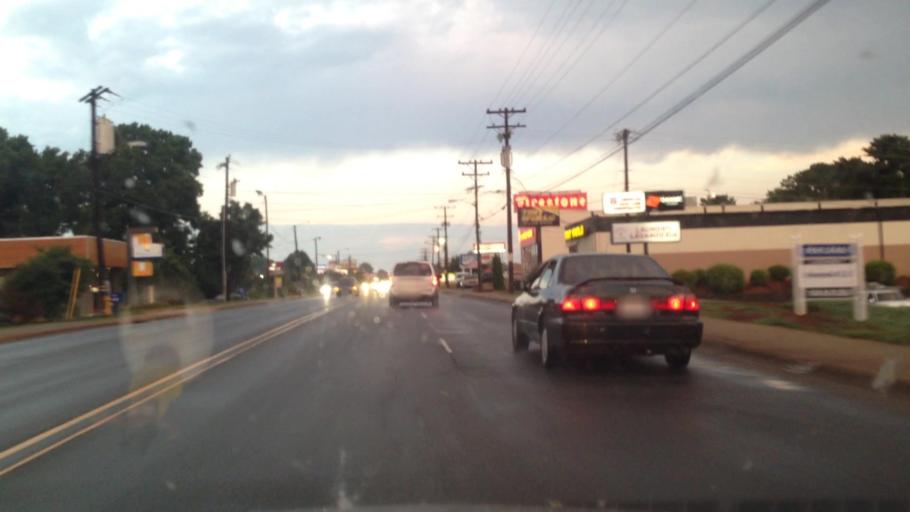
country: US
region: North Carolina
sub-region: Mecklenburg County
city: Pineville
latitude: 35.1475
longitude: -80.8764
